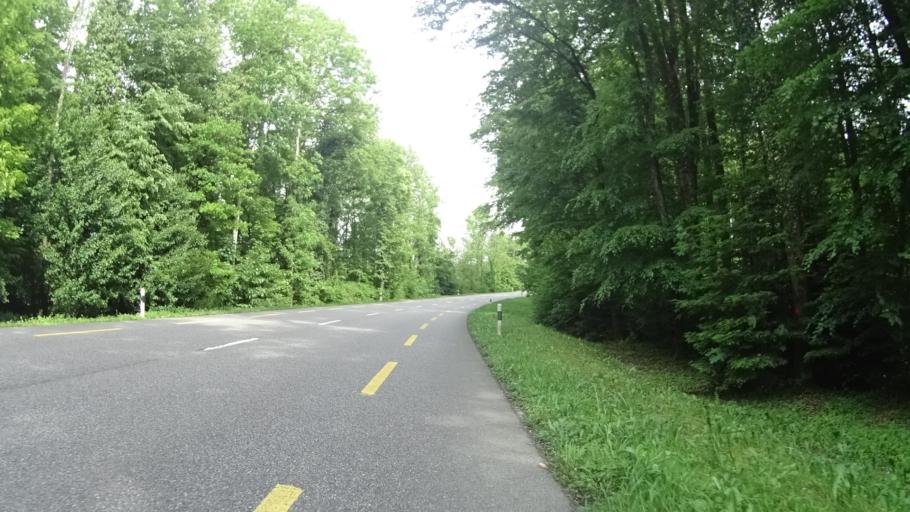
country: DE
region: Baden-Wuerttemberg
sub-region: Freiburg Region
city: Murg
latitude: 47.5530
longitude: 8.0074
